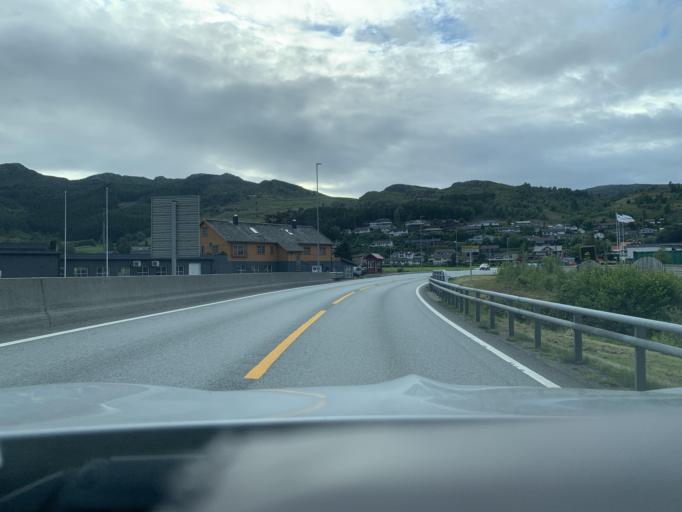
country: NO
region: Rogaland
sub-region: Bjerkreim
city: Vikesa
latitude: 58.6299
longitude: 6.0796
